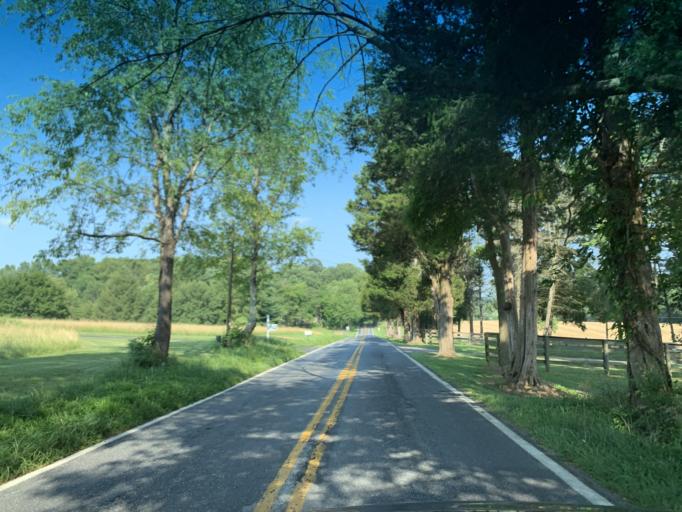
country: US
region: Maryland
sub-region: Frederick County
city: Urbana
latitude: 39.2502
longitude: -77.3692
